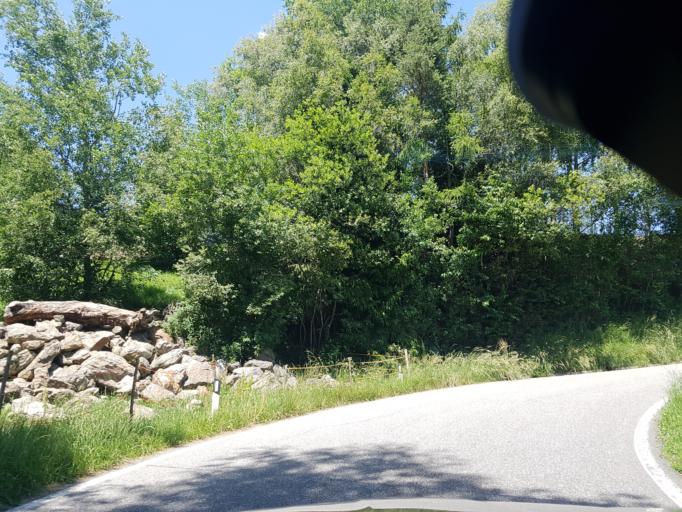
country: IT
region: Trentino-Alto Adige
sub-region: Bolzano
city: Villandro - Villanders
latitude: 46.6370
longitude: 11.5289
